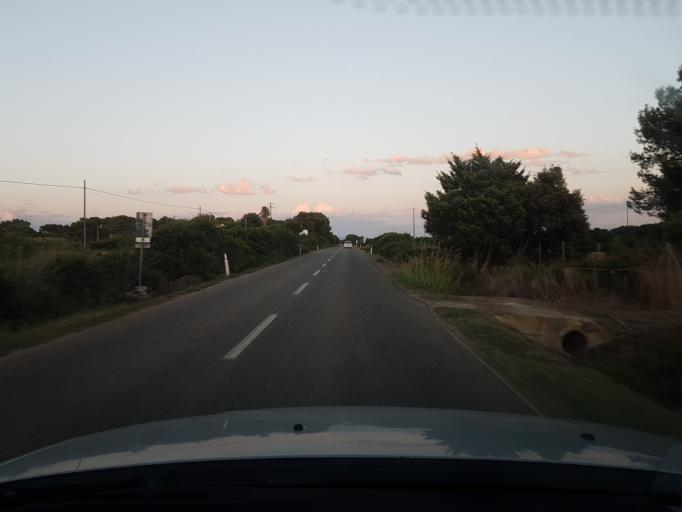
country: IT
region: Sardinia
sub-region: Provincia di Oristano
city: Riola Sardo
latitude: 40.0227
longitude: 8.4487
